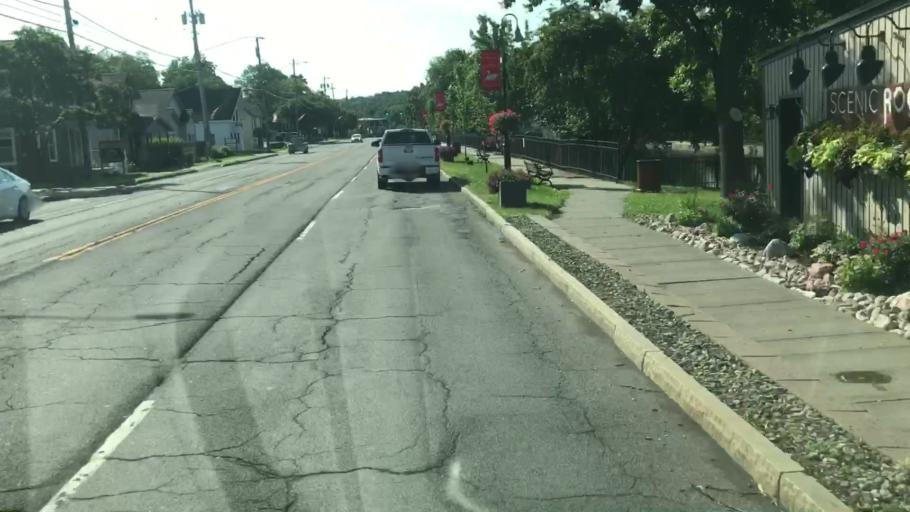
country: US
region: New York
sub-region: Onondaga County
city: Manlius
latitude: 43.0039
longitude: -75.9822
